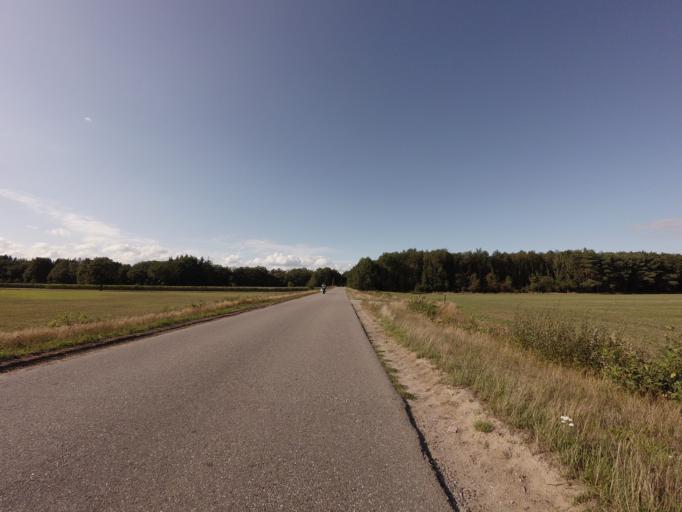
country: NL
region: Friesland
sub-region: Gemeente Heerenveen
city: Jubbega
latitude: 52.9803
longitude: 6.1831
